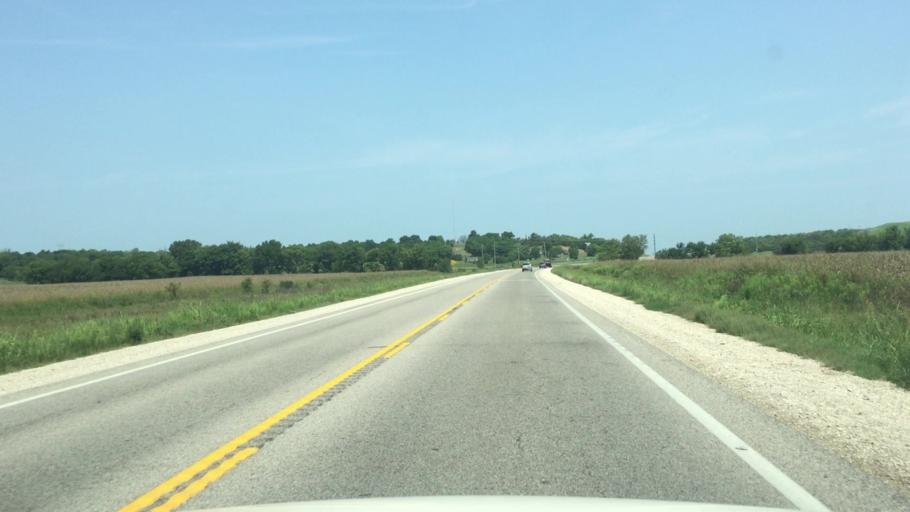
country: US
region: Kansas
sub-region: Montgomery County
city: Cherryvale
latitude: 37.2028
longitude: -95.5840
